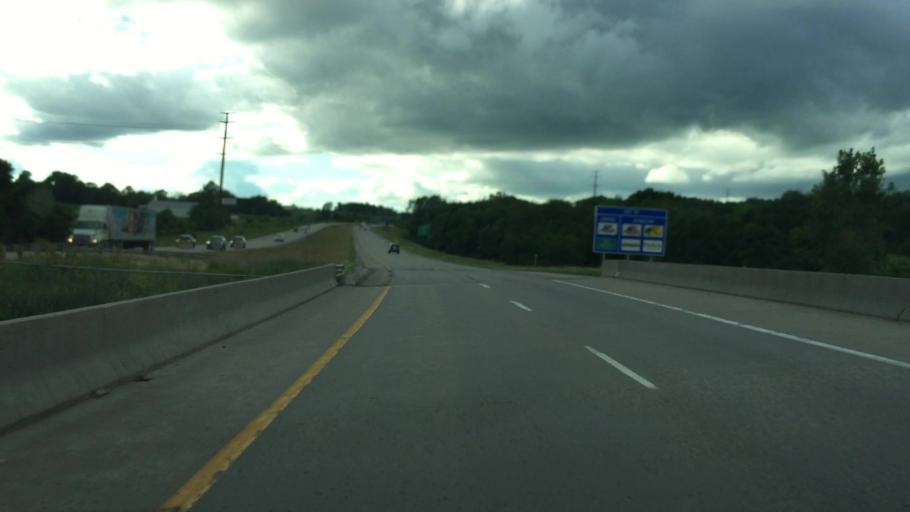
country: US
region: Iowa
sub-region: Polk County
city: Altoona
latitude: 41.6240
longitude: -93.4946
